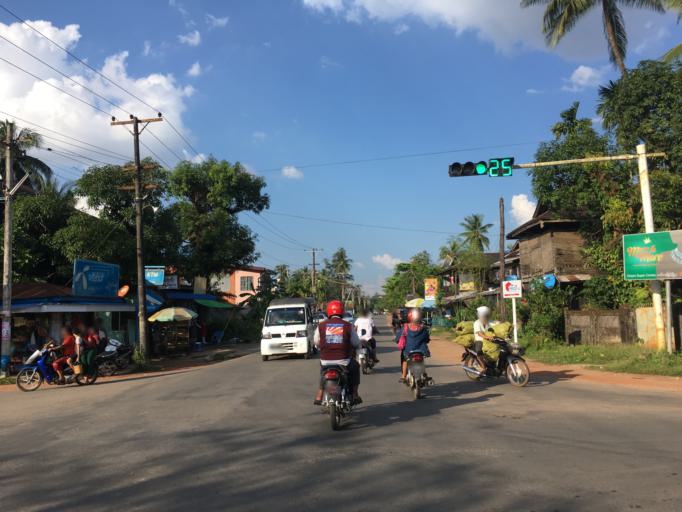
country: MM
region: Mon
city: Mawlamyine
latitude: 16.4510
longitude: 97.6245
